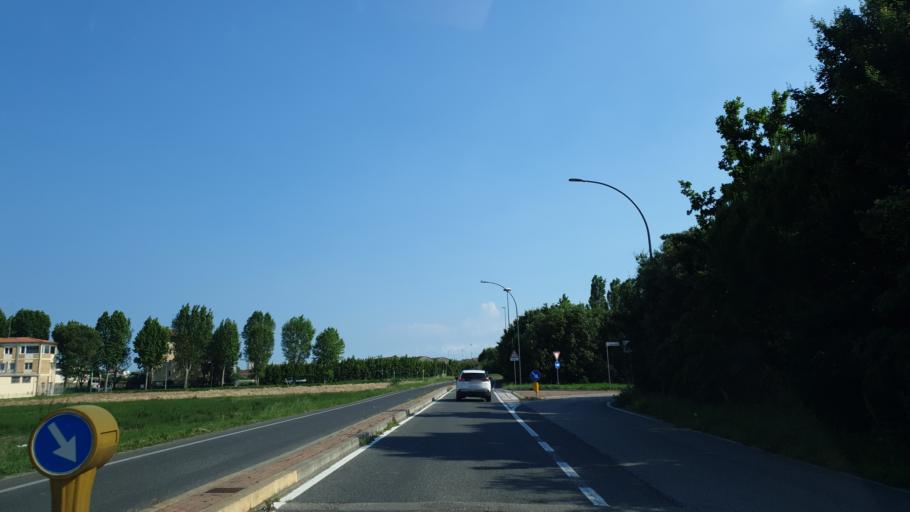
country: IT
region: Emilia-Romagna
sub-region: Provincia di Ravenna
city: Ravenna
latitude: 44.4291
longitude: 12.2149
